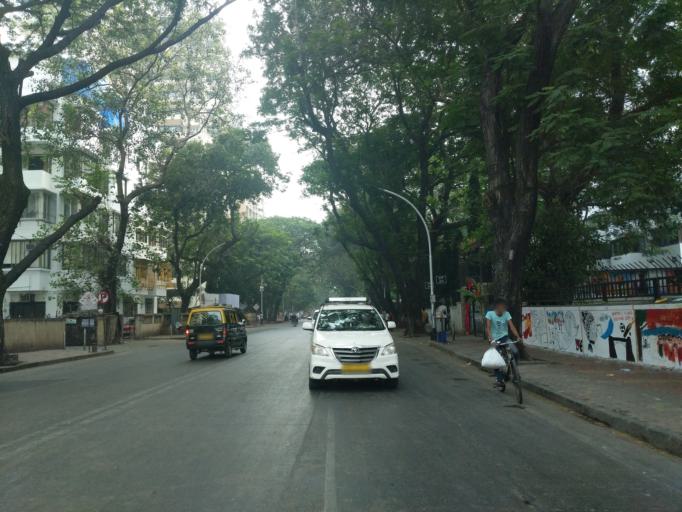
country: IN
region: Maharashtra
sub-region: Raigarh
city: Uran
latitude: 18.9259
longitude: 72.8269
